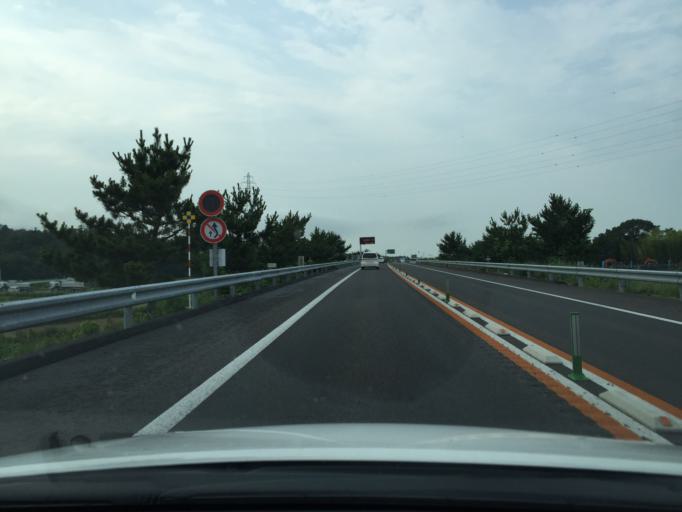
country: JP
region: Fukushima
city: Namie
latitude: 37.3693
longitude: 140.9672
